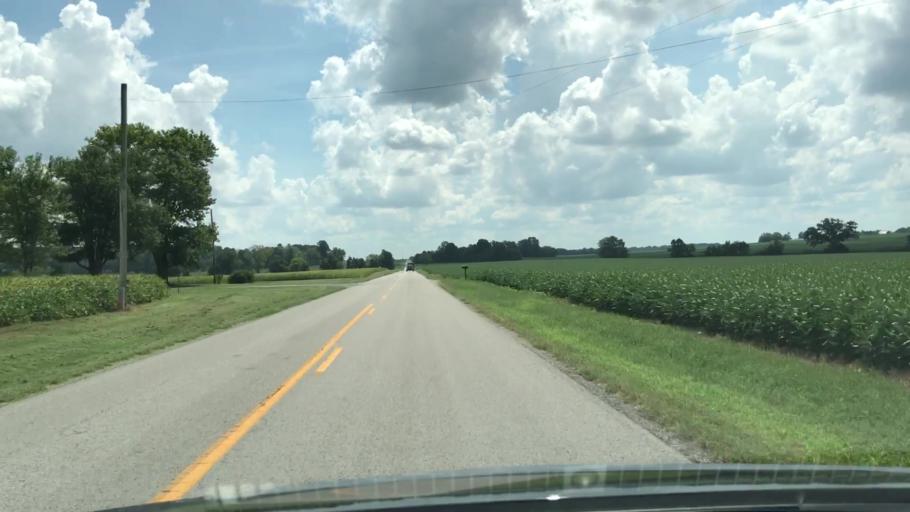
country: US
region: Kentucky
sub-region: Todd County
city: Guthrie
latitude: 36.7057
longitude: -87.0456
